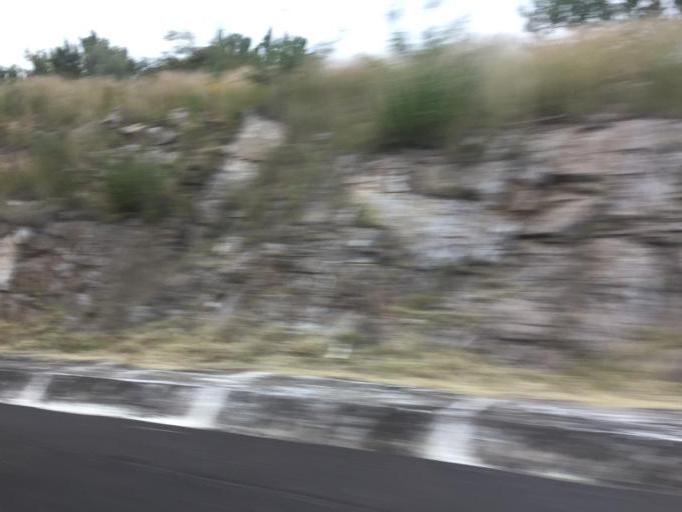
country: MX
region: Jalisco
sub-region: Zapotlan del Rey
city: Zapotlan del Rey
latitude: 20.4741
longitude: -102.9249
